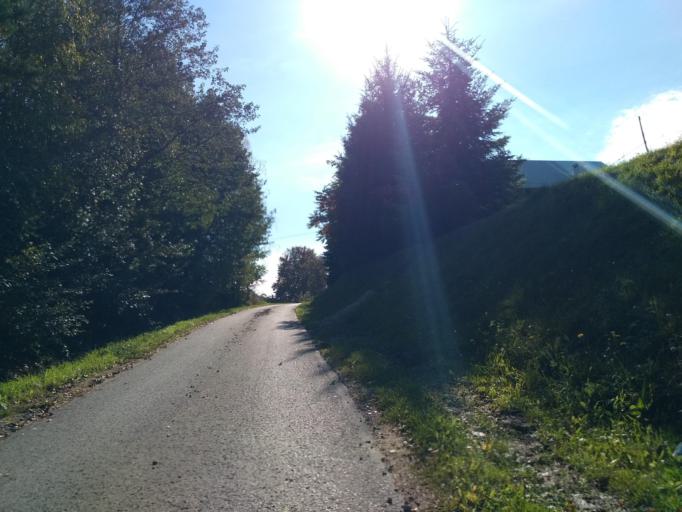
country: PL
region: Subcarpathian Voivodeship
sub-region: Powiat debicki
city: Slotowa
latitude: 49.9376
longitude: 21.2782
